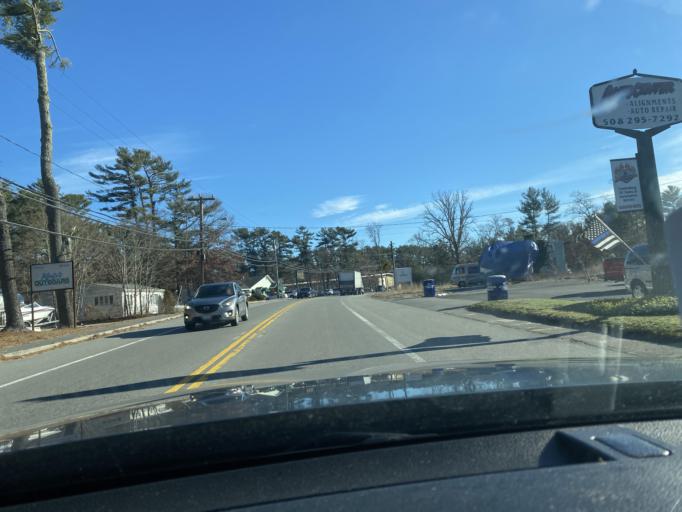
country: US
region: Massachusetts
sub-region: Plymouth County
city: West Wareham
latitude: 41.7905
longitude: -70.7530
